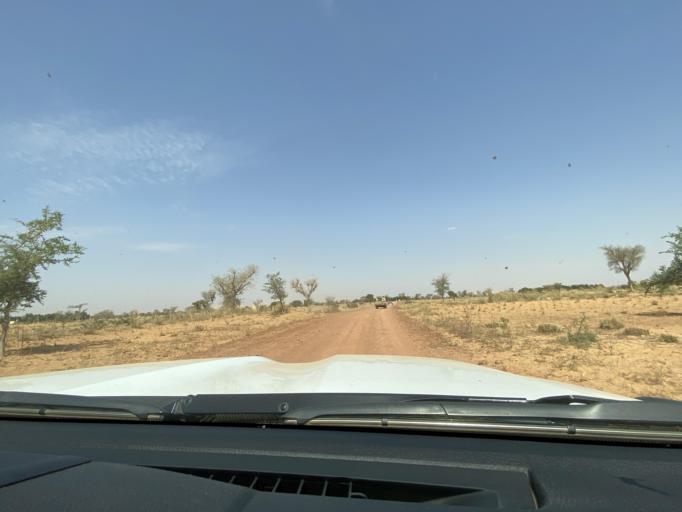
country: NE
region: Dosso
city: Birnin Gaoure
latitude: 13.2361
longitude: 2.8676
